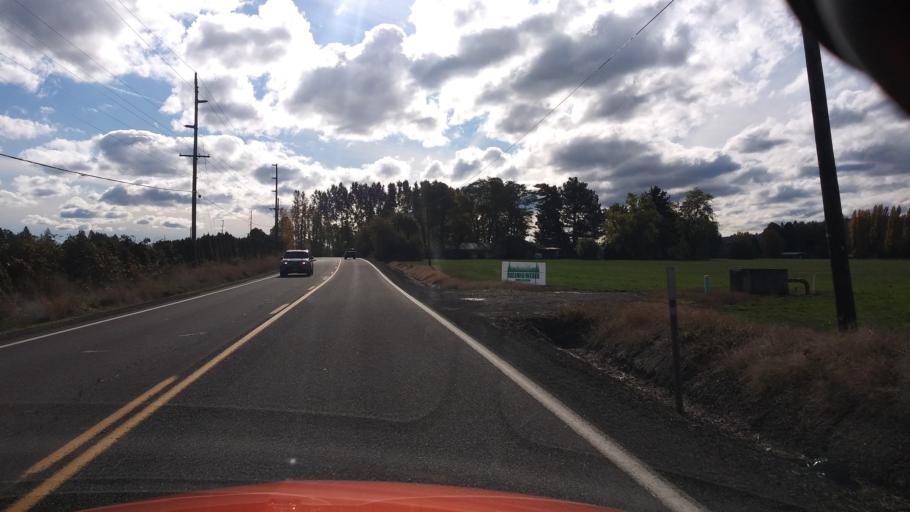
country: US
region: Oregon
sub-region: Washington County
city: Banks
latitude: 45.5848
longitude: -123.1144
